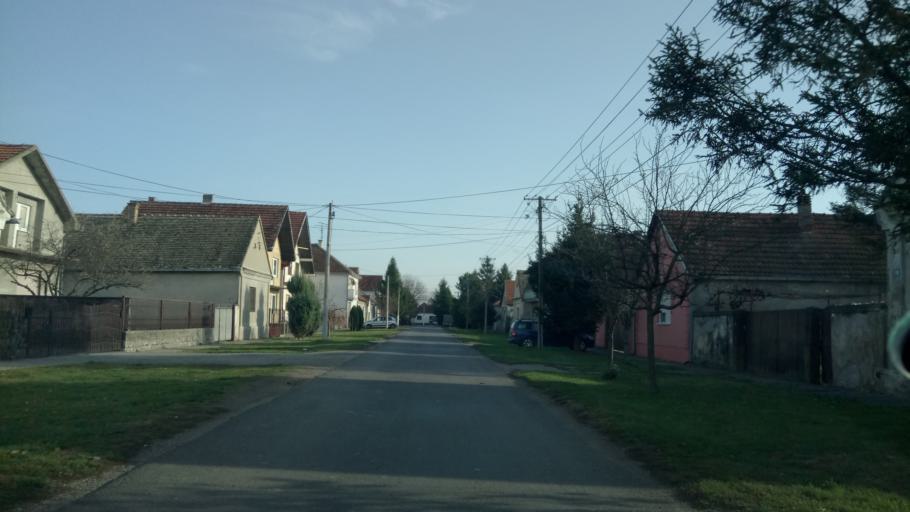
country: RS
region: Autonomna Pokrajina Vojvodina
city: Nova Pazova
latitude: 44.9487
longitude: 20.2313
